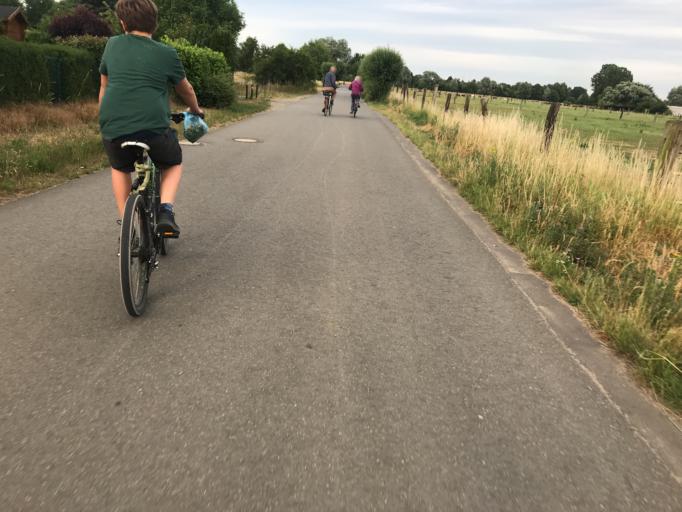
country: DE
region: Lower Saxony
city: Isernhagen Farster Bauerschaft
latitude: 52.4177
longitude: 9.8096
